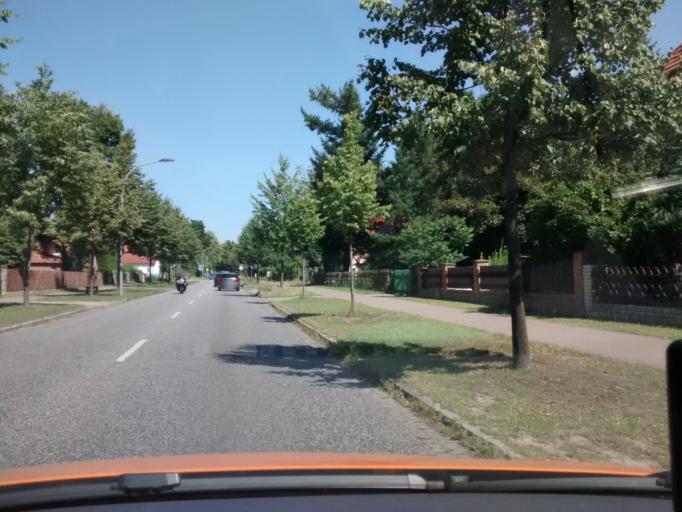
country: DE
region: Brandenburg
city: Birkenwerder
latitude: 52.6824
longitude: 13.2819
